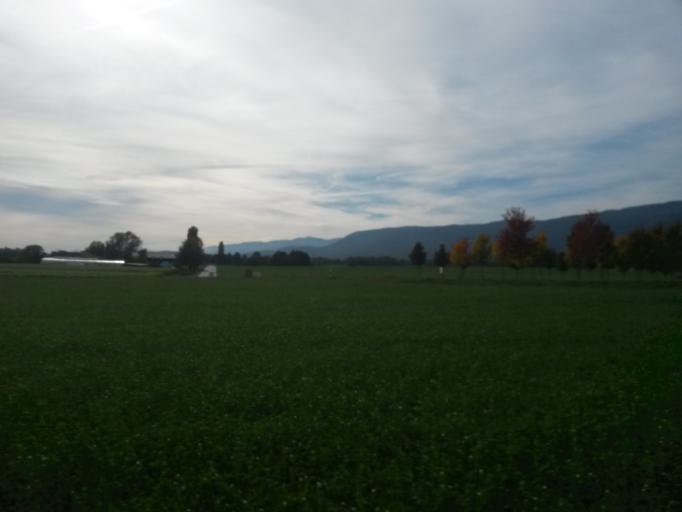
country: CH
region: Vaud
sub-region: Nyon District
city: Trelex
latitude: 46.4126
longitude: 6.2060
